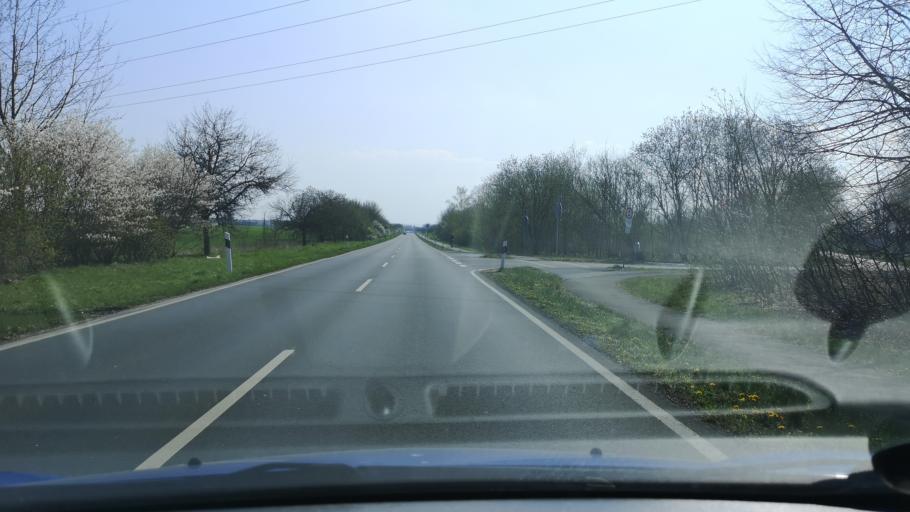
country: DE
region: Lower Saxony
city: Neustadt am Rubenberge
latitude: 52.5222
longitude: 9.4766
